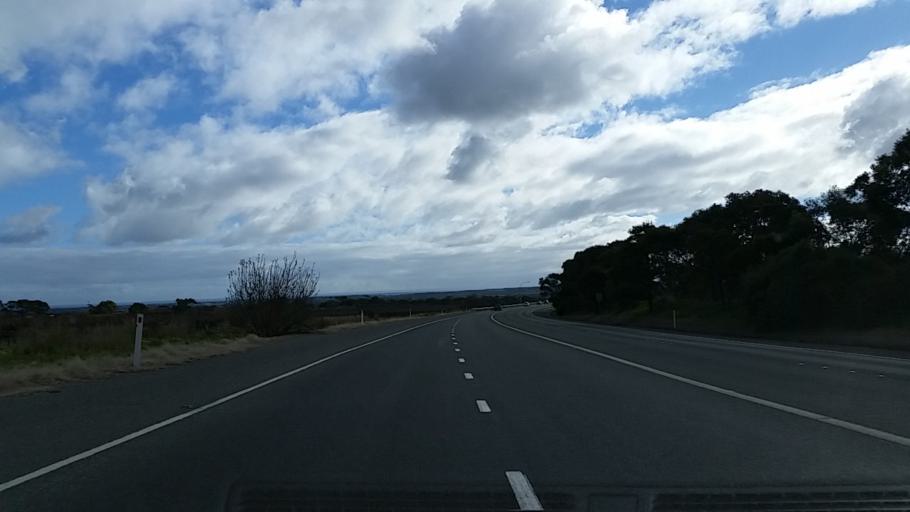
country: AU
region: South Australia
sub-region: Onkaparinga
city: McLaren Vale
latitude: -35.2778
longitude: 138.5469
